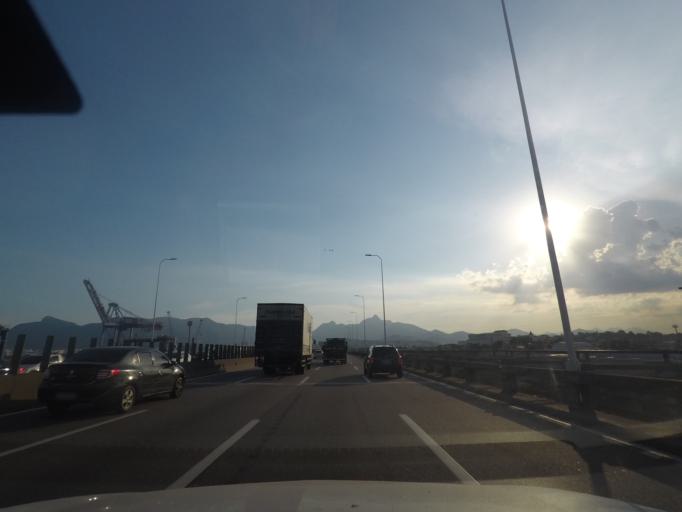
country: BR
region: Rio de Janeiro
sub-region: Rio De Janeiro
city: Rio de Janeiro
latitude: -22.8765
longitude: -43.2082
